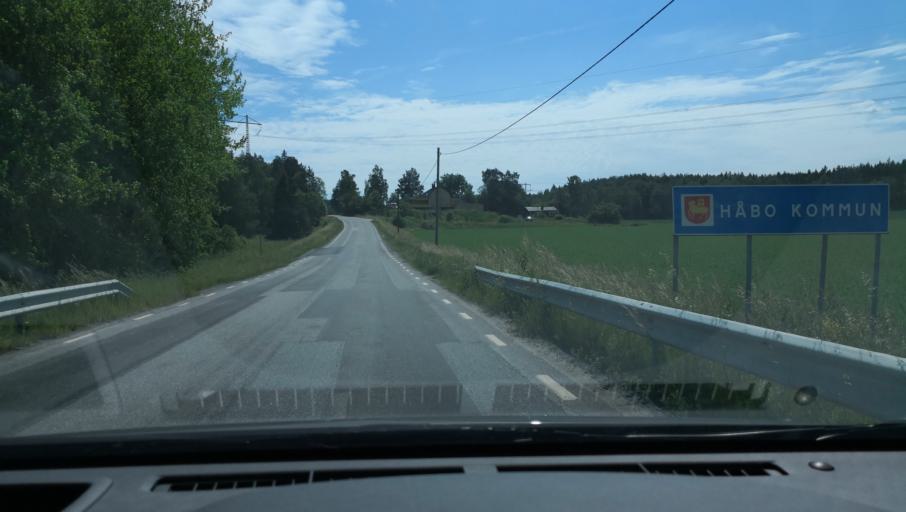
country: SE
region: Uppsala
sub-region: Habo Kommun
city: Balsta
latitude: 59.6621
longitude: 17.4498
